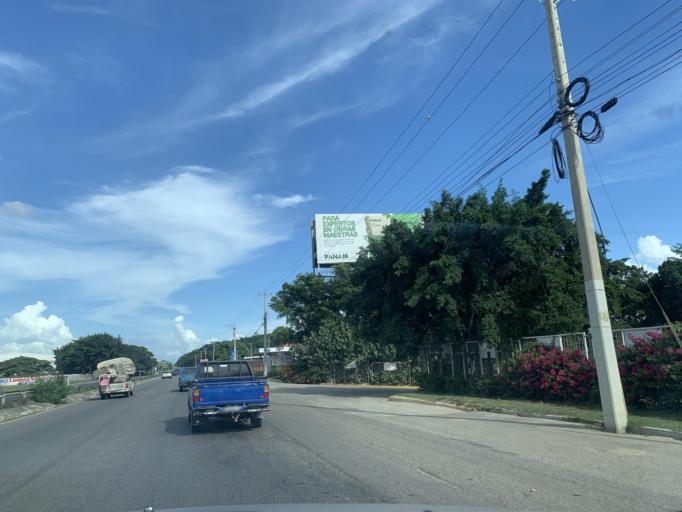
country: DO
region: Santiago
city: Villa Gonzalez
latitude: 19.5404
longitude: -70.7961
